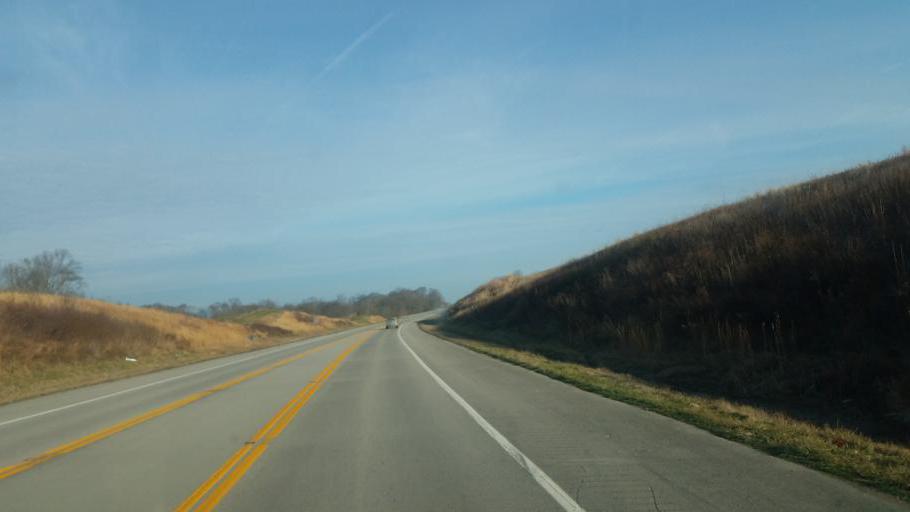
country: US
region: Kentucky
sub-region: Russell County
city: Jamestown
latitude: 36.9819
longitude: -85.0861
